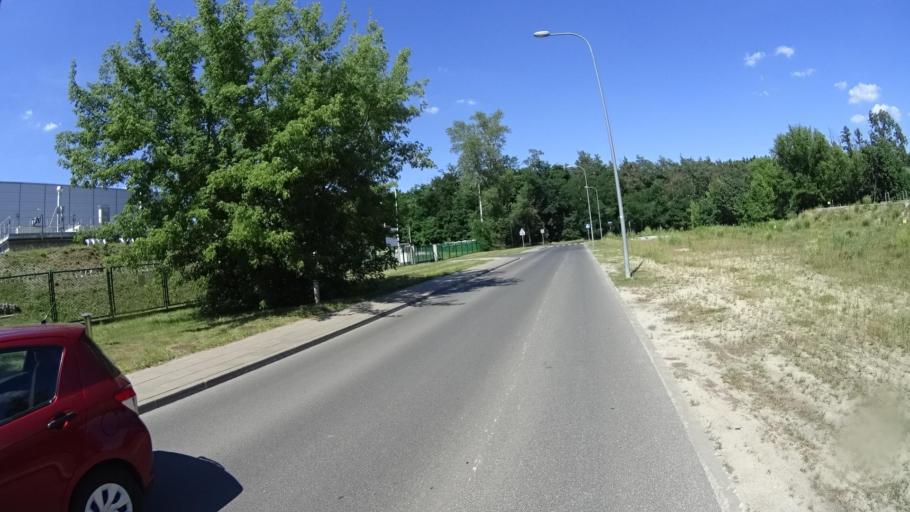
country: PL
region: Masovian Voivodeship
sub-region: Warszawa
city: Bialoleka
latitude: 52.3521
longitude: 20.9670
